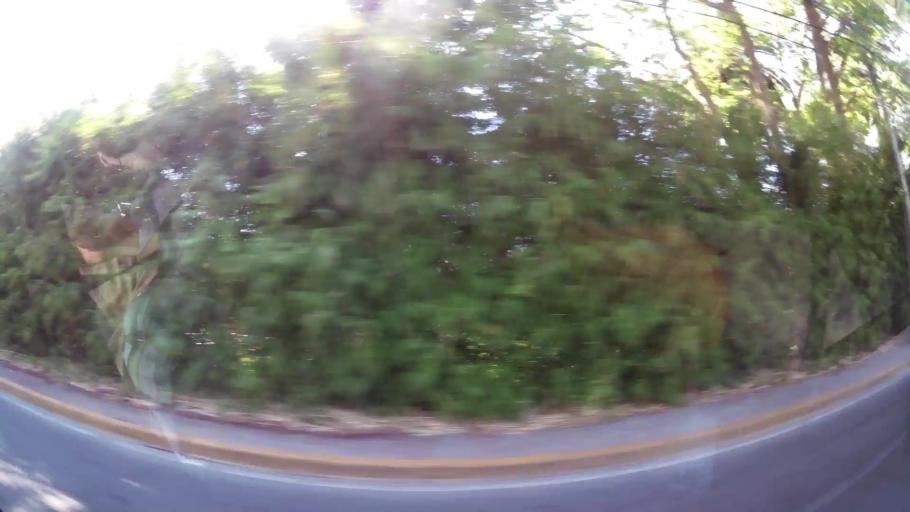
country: AR
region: Buenos Aires
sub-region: Partido de Tigre
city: Tigre
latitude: -34.4305
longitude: -58.5843
